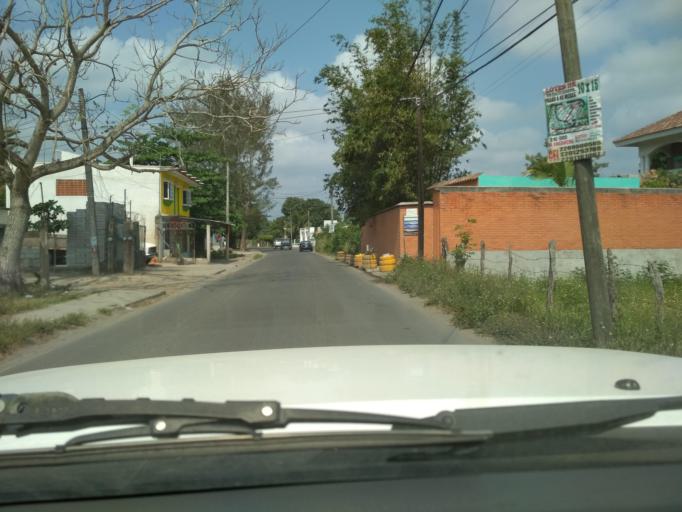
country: MX
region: Veracruz
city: El Tejar
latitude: 19.0762
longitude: -96.1665
